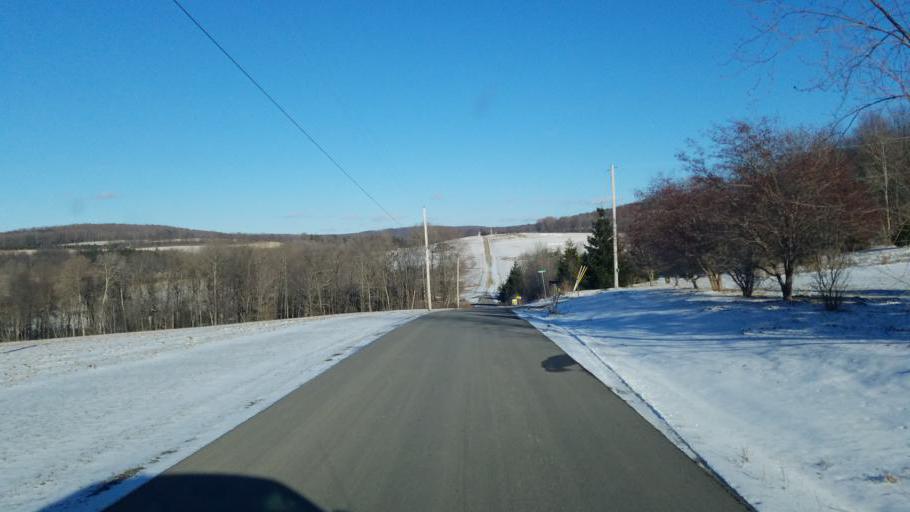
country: US
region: Pennsylvania
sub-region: Potter County
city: Galeton
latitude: 41.9014
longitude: -77.7493
